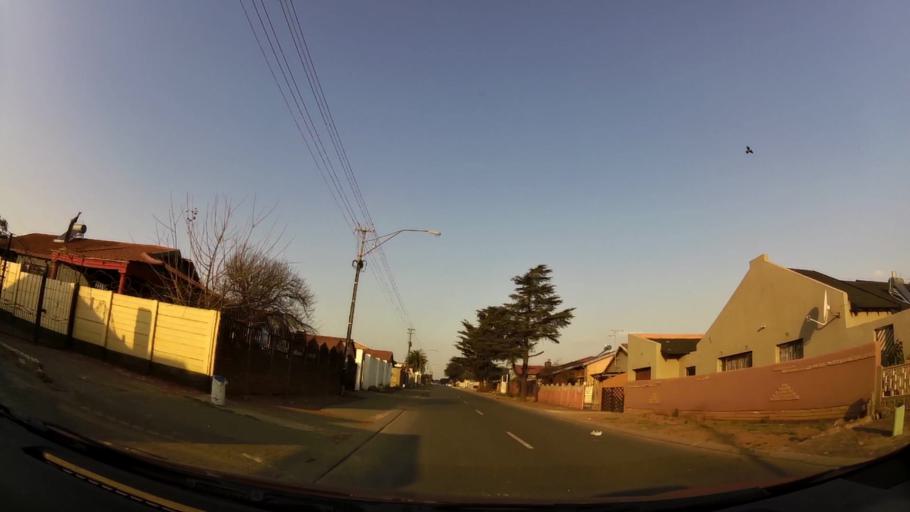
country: ZA
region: Gauteng
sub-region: City of Johannesburg Metropolitan Municipality
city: Soweto
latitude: -26.2800
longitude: 27.8941
